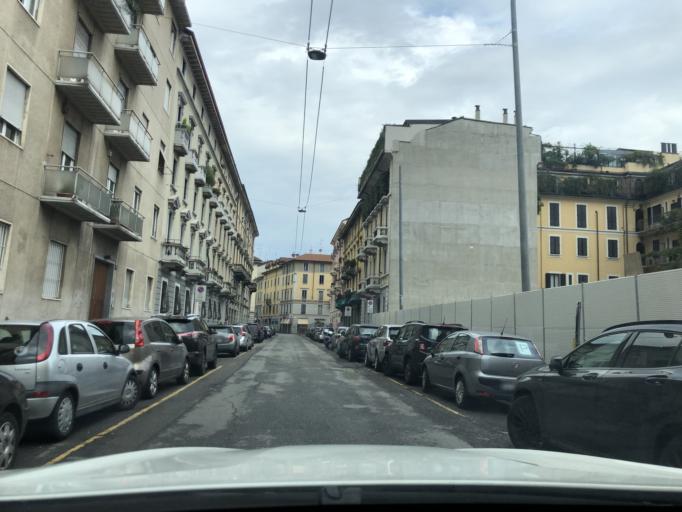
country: IT
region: Lombardy
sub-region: Citta metropolitana di Milano
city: Milano
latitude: 45.4712
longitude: 9.2085
